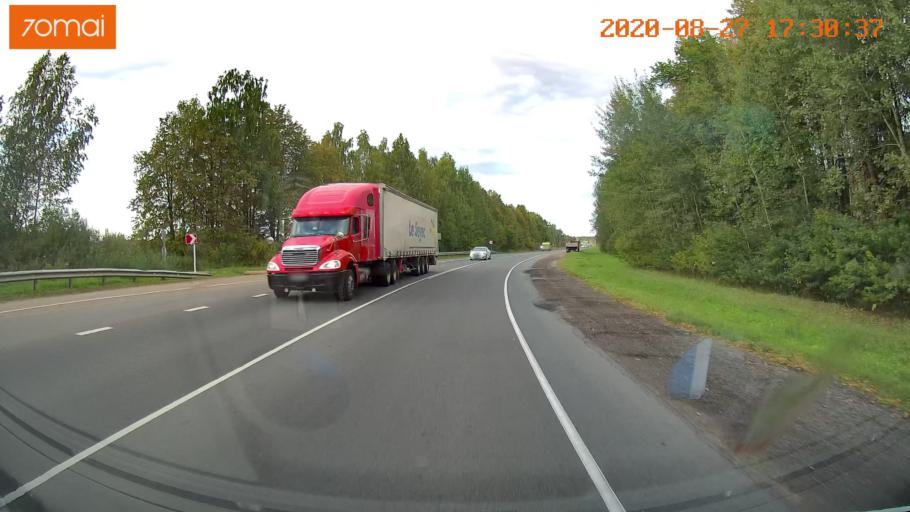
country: RU
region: Ivanovo
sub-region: Gorod Ivanovo
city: Ivanovo
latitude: 56.9071
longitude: 40.9446
